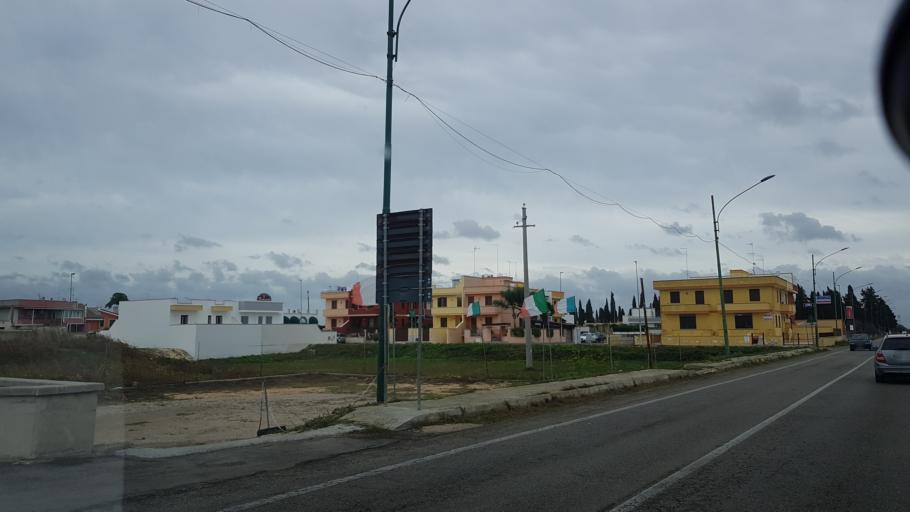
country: IT
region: Apulia
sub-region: Provincia di Lecce
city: Guagnano
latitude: 40.4012
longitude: 17.9556
